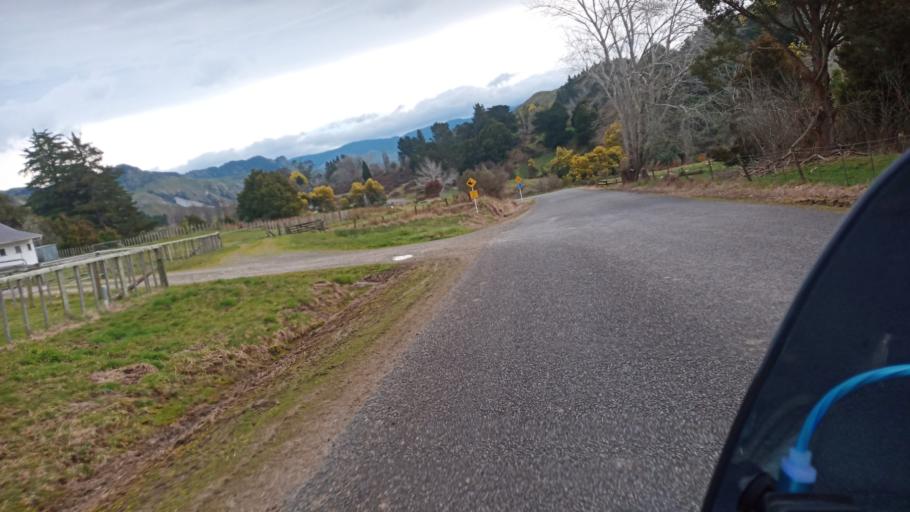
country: NZ
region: Hawke's Bay
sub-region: Wairoa District
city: Wairoa
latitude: -38.7692
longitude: 177.4079
